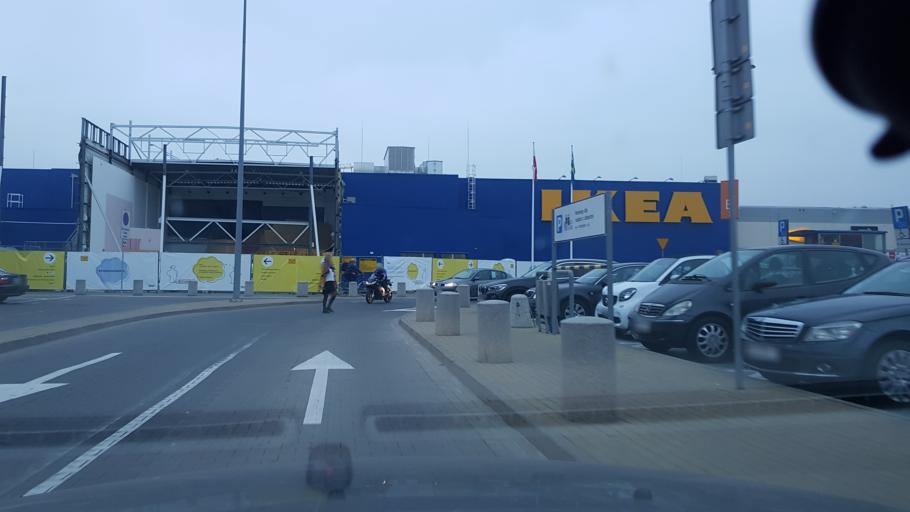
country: PL
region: Masovian Voivodeship
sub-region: Powiat pruszkowski
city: Nowe Grocholice
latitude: 52.1334
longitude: 20.8965
